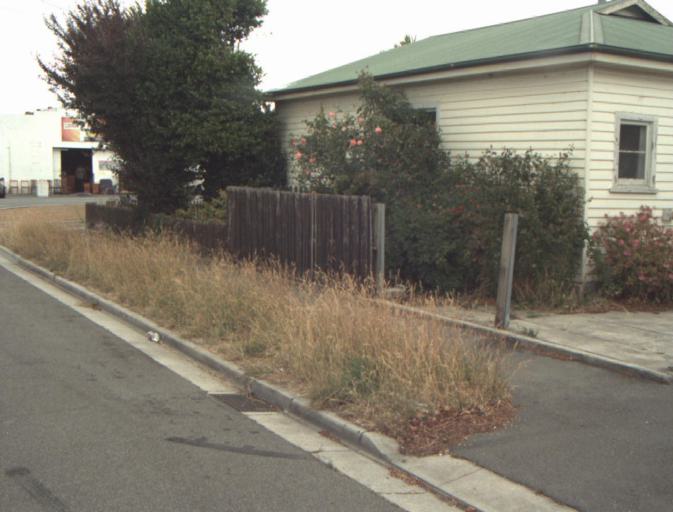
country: AU
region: Tasmania
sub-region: Launceston
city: Launceston
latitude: -41.4248
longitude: 147.1324
